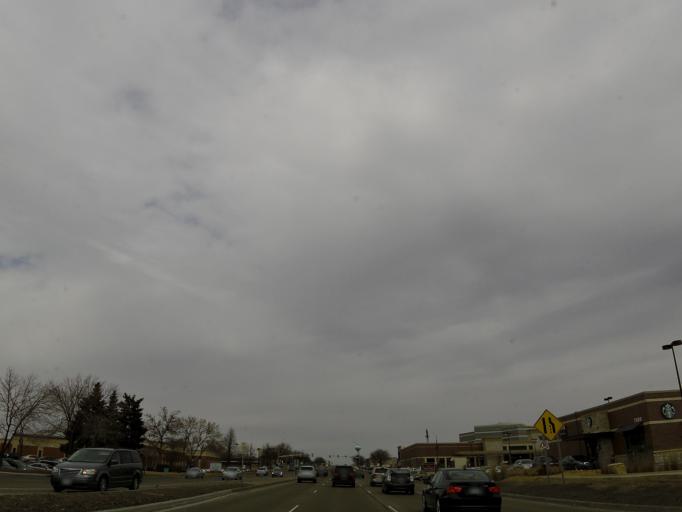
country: US
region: Minnesota
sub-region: Hennepin County
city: Edina
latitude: 44.8661
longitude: -93.3288
